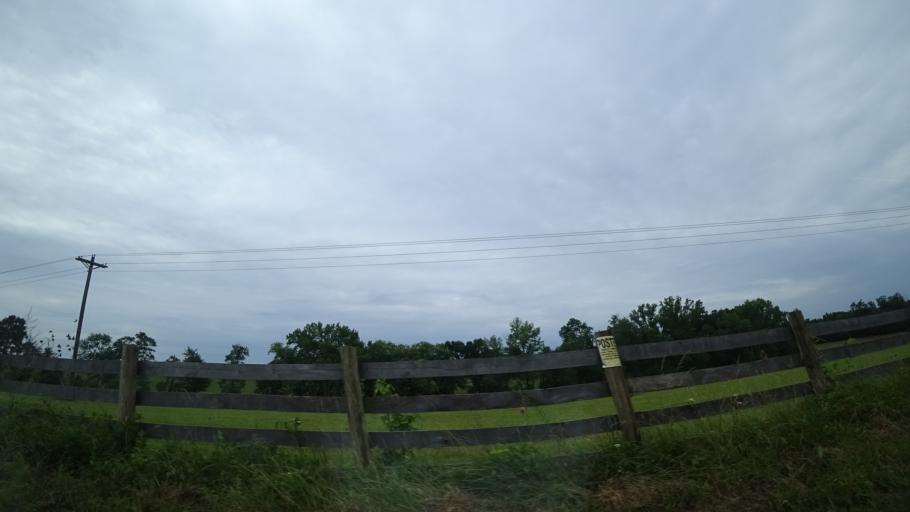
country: US
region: Virginia
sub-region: Spotsylvania County
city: Spotsylvania
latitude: 38.1236
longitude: -77.7726
